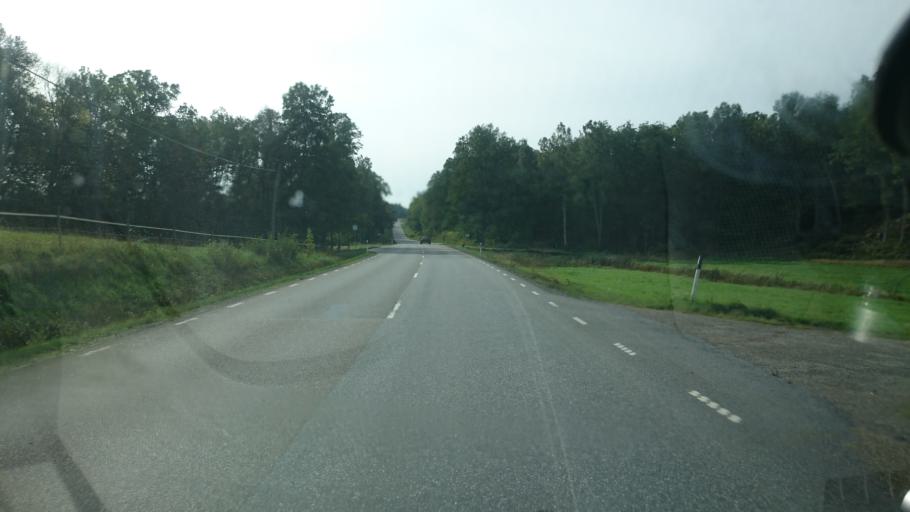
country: SE
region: Vaestra Goetaland
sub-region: Alingsas Kommun
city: Sollebrunn
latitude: 58.0435
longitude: 12.4668
